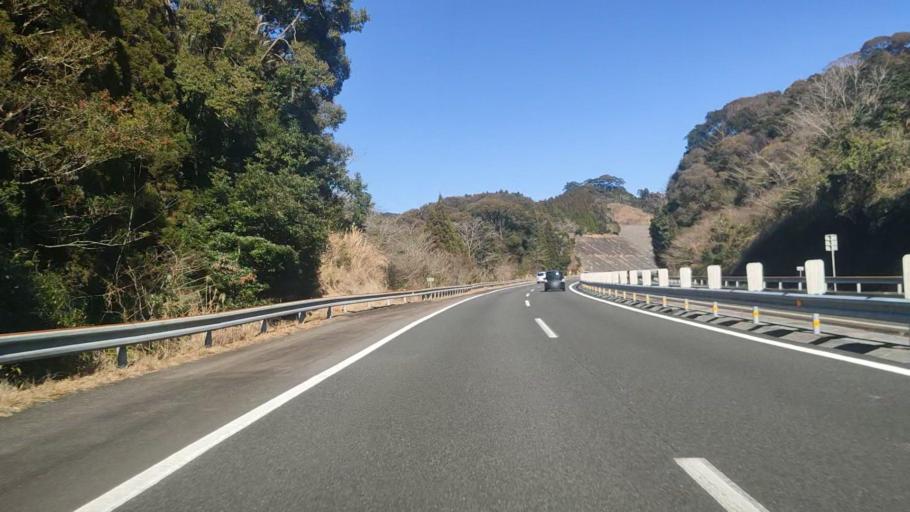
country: JP
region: Miyazaki
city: Miyakonojo
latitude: 31.8185
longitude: 131.2167
